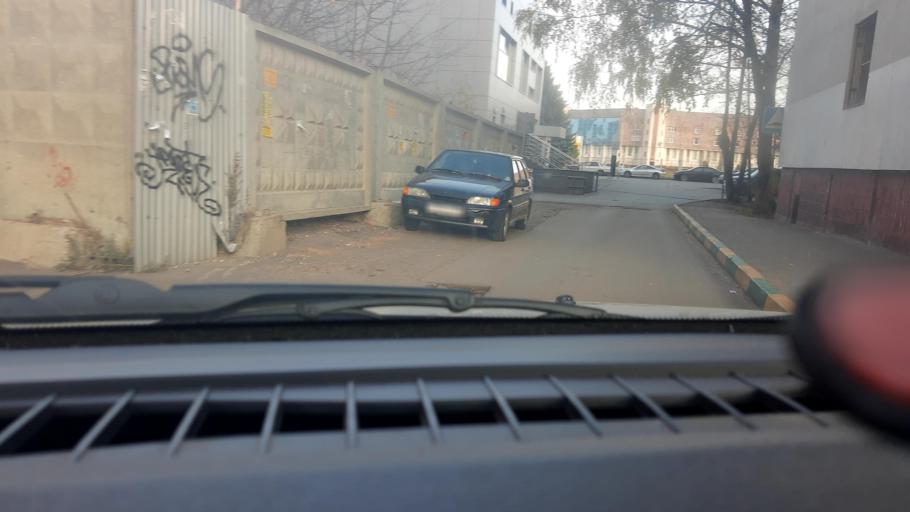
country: RU
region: Nizjnij Novgorod
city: Afonino
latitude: 56.2977
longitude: 44.0762
